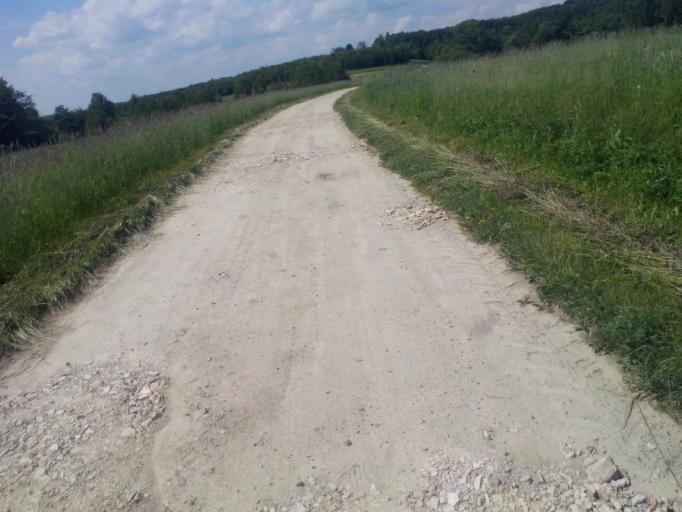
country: PL
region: Subcarpathian Voivodeship
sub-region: Powiat strzyzowski
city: Jawornik
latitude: 49.8445
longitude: 21.8521
